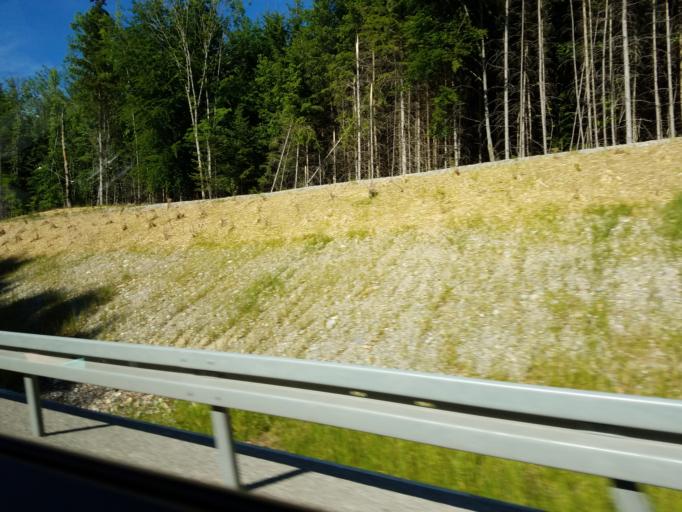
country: DE
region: Bavaria
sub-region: Upper Bavaria
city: Pocking
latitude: 48.0011
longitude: 11.2938
